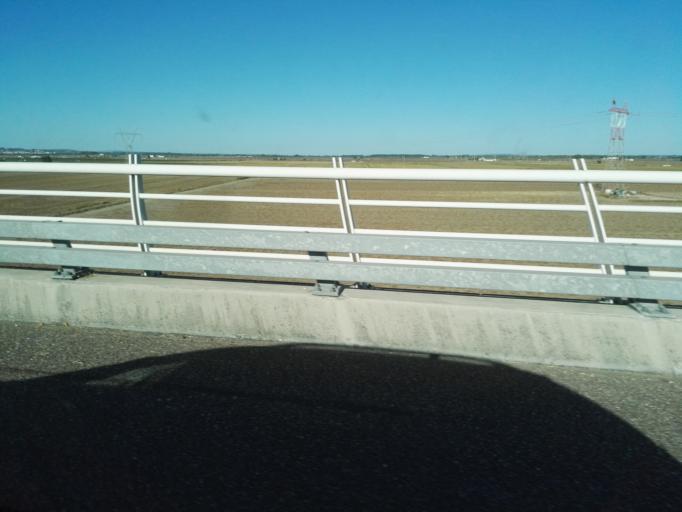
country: PT
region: Santarem
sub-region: Benavente
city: Samora Correia
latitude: 38.9876
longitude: -8.8915
